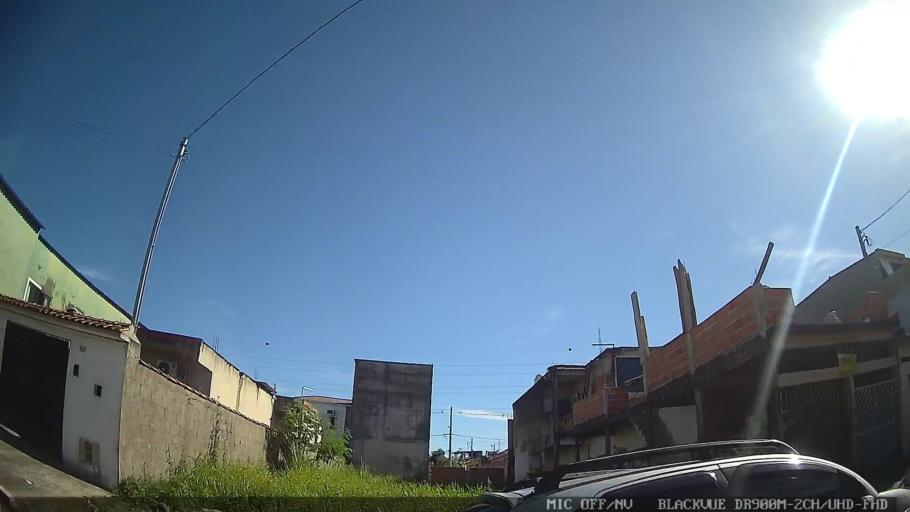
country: BR
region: Sao Paulo
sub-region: Santos
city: Santos
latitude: -23.9338
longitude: -46.2870
